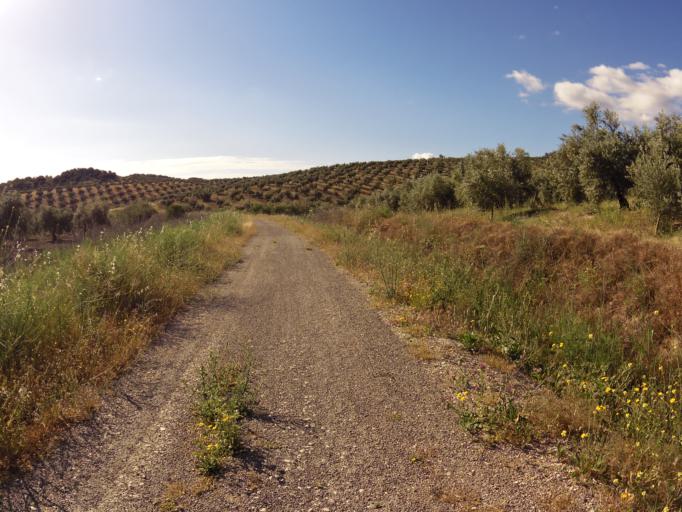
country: ES
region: Andalusia
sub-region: Province of Cordoba
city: Fuente-Tojar
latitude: 37.5794
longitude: -4.1843
